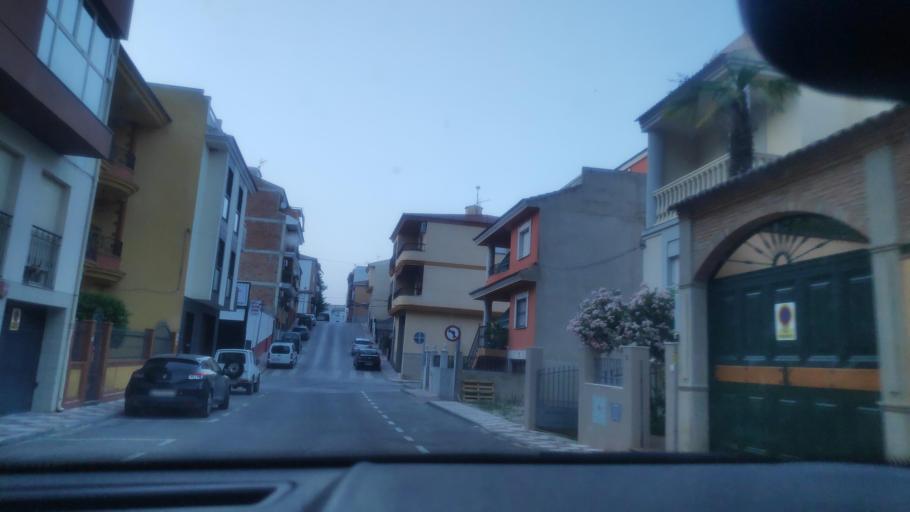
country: ES
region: Andalusia
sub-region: Provincia de Jaen
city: Mancha Real
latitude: 37.7839
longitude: -3.6052
